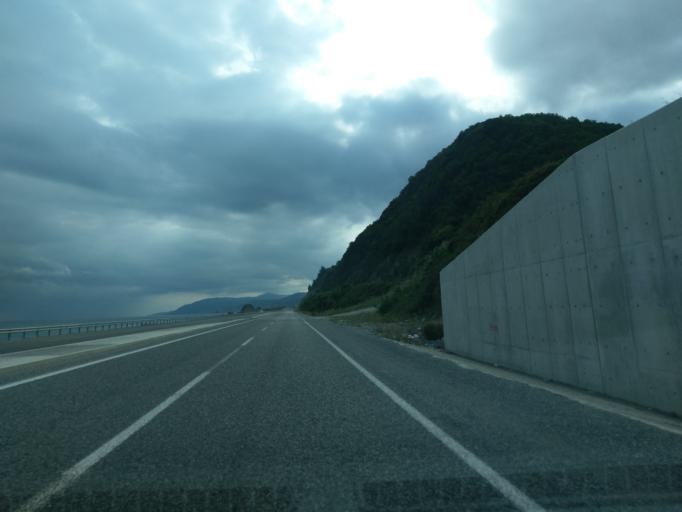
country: TR
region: Kastamonu
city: Catalzeytin
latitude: 41.9475
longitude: 34.2628
